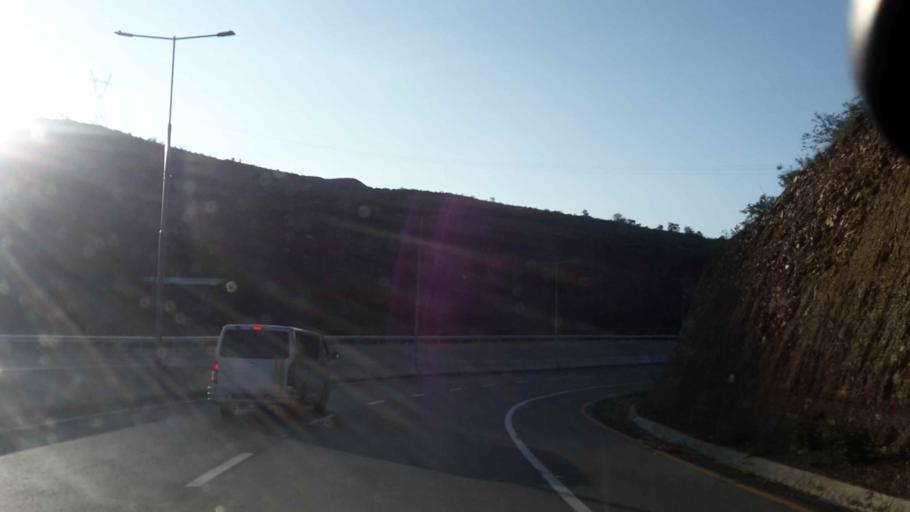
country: BO
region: Cochabamba
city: Tarata
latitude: -17.5012
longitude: -66.0921
